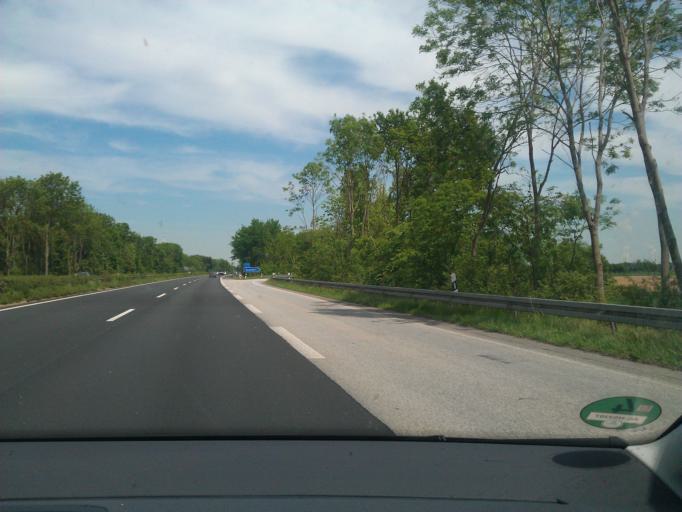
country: DE
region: North Rhine-Westphalia
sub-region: Regierungsbezirk Koln
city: Titz
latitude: 51.0053
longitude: 6.4001
